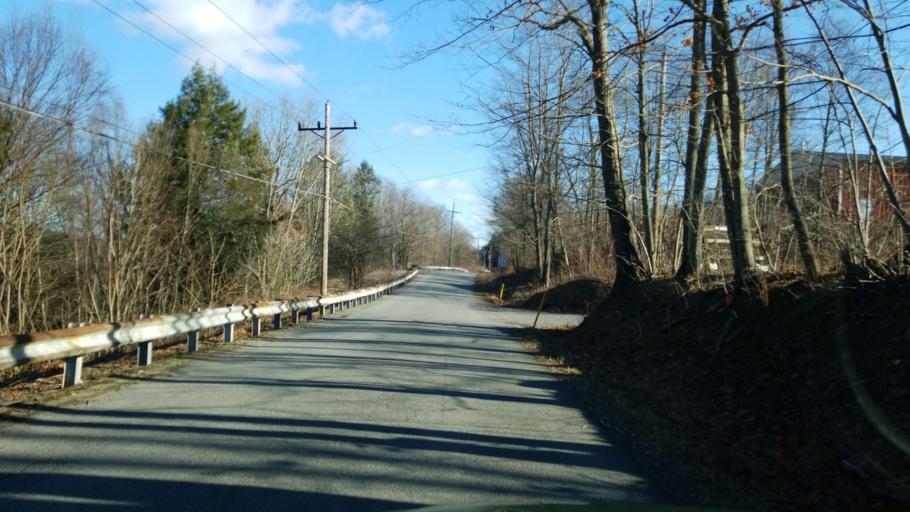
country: US
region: Pennsylvania
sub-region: Clearfield County
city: Hyde
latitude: 40.9841
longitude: -78.4813
